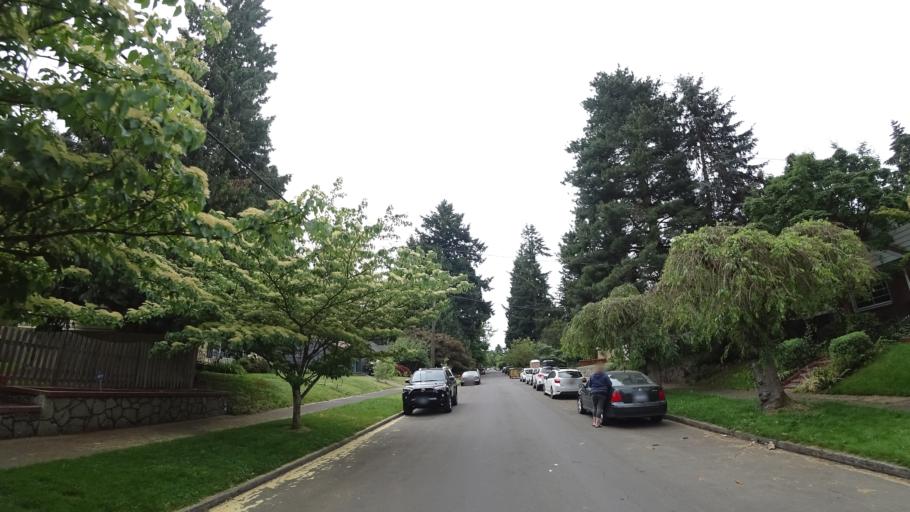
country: US
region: Oregon
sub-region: Multnomah County
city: Portland
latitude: 45.5678
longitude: -122.6318
